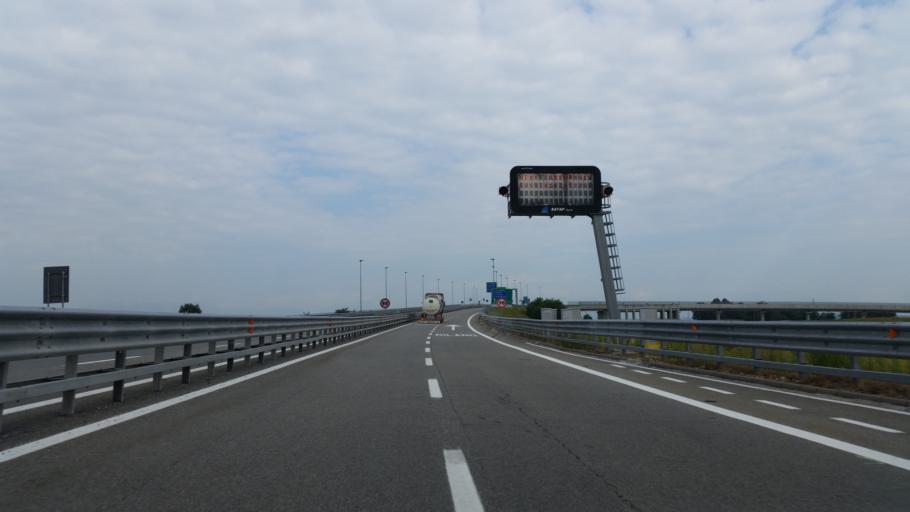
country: IT
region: Piedmont
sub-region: Provincia di Torino
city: Chivasso
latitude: 45.2185
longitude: 7.9236
